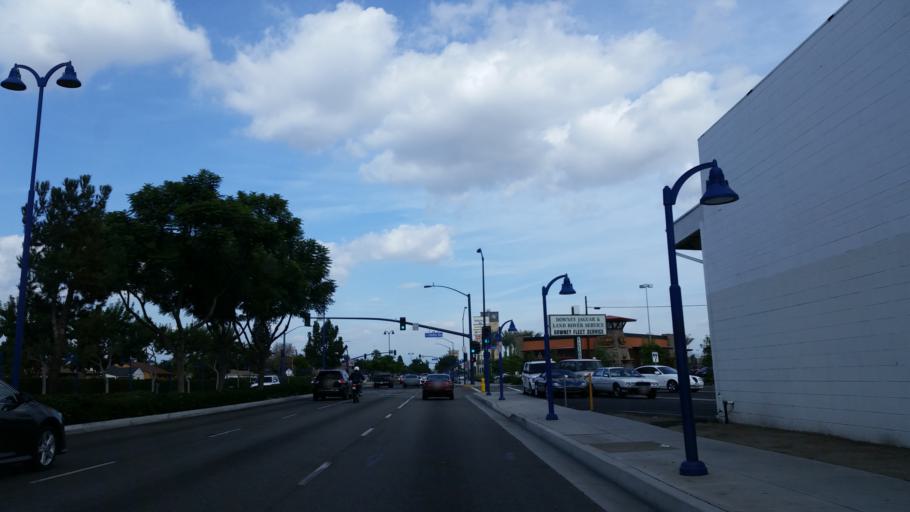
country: US
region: California
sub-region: Los Angeles County
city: Downey
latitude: 33.9210
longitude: -118.1347
